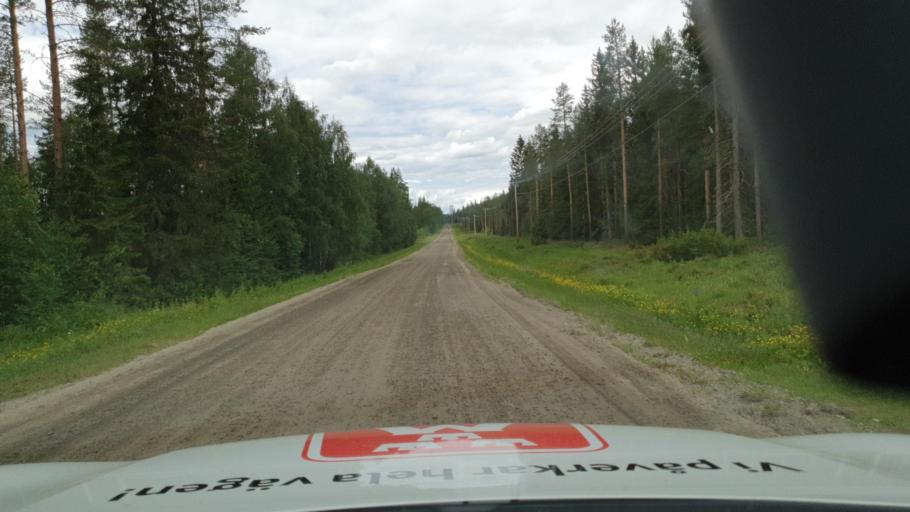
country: SE
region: Vaesterbotten
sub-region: Bjurholms Kommun
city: Bjurholm
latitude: 63.8512
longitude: 18.9827
